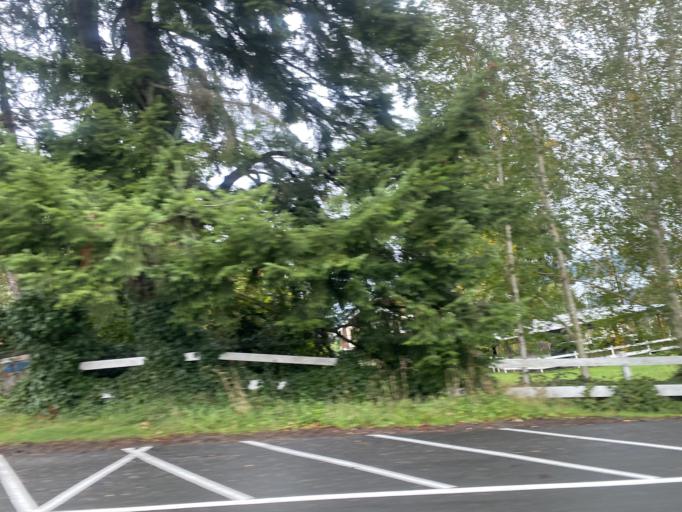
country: US
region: Washington
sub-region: Island County
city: Langley
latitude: 48.0400
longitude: -122.4108
